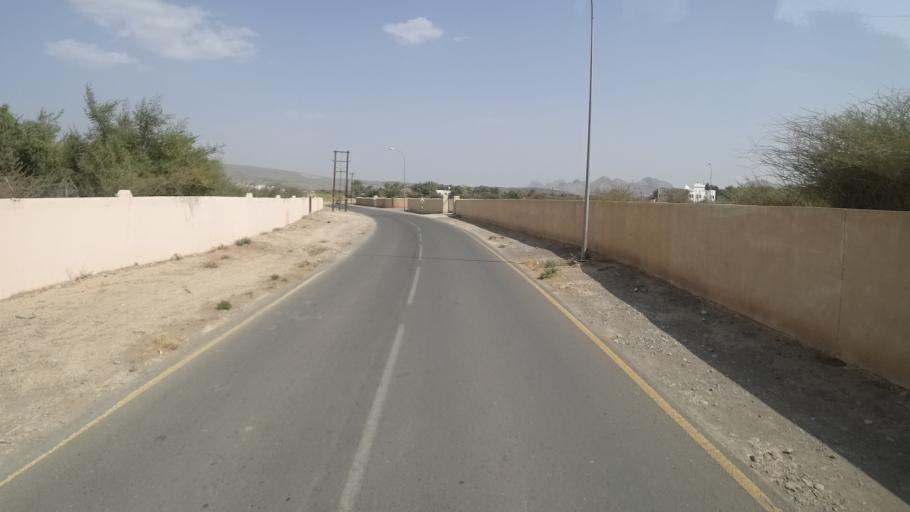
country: OM
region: Muhafazat ad Dakhiliyah
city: Bahla'
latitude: 23.1070
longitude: 57.2968
